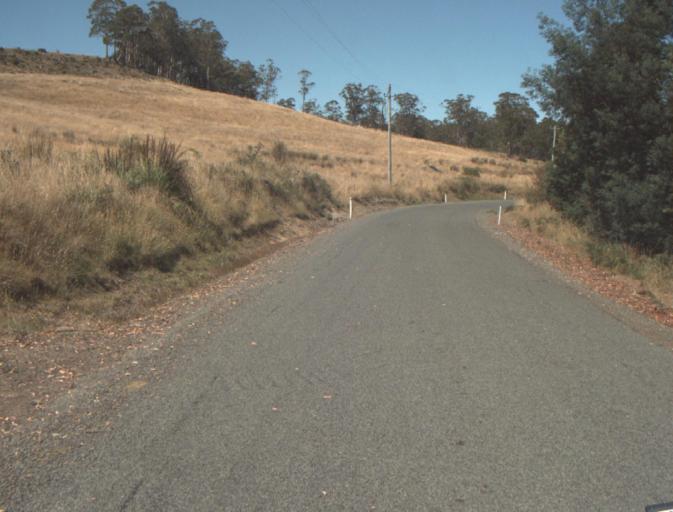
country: AU
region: Tasmania
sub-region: Launceston
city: Newstead
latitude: -41.3572
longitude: 147.3029
